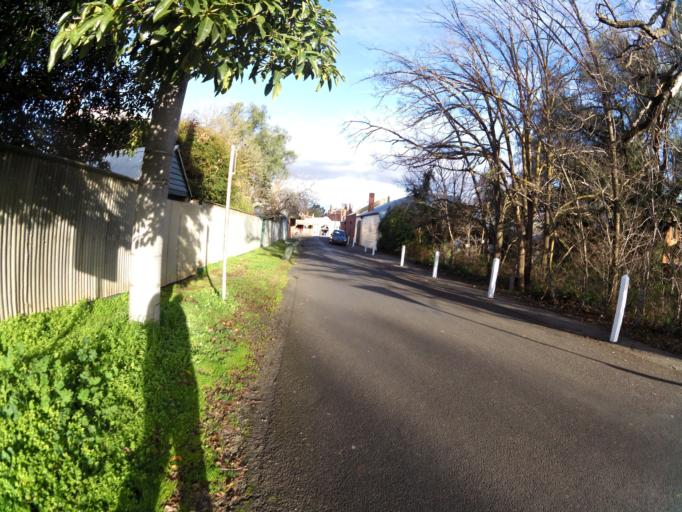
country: AU
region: Victoria
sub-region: Mount Alexander
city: Castlemaine
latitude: -36.9961
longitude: 144.0692
